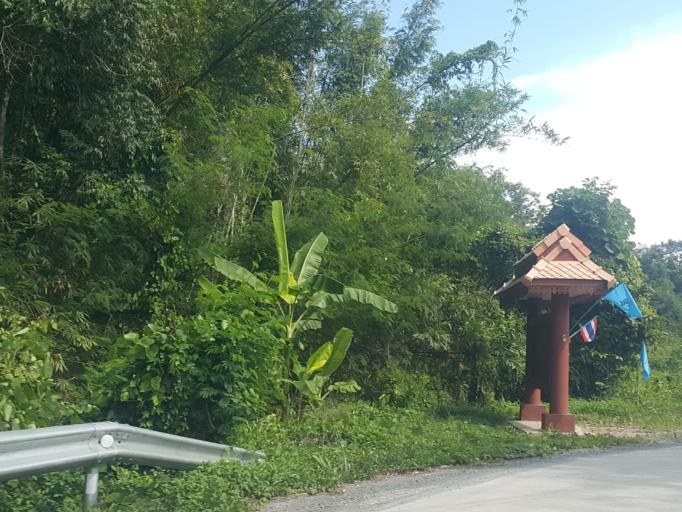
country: TH
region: Chiang Mai
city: Mae On
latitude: 18.8117
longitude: 99.2283
